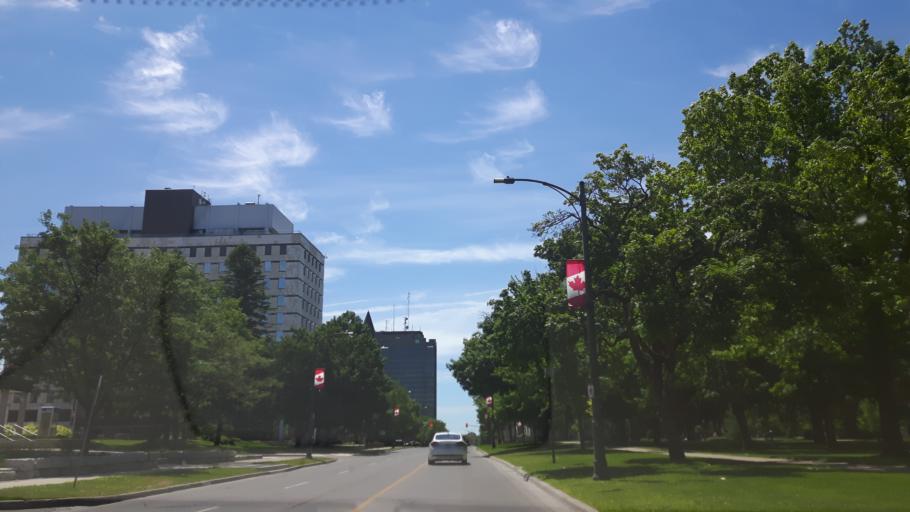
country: CA
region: Ontario
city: London
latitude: 42.9892
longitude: -81.2475
